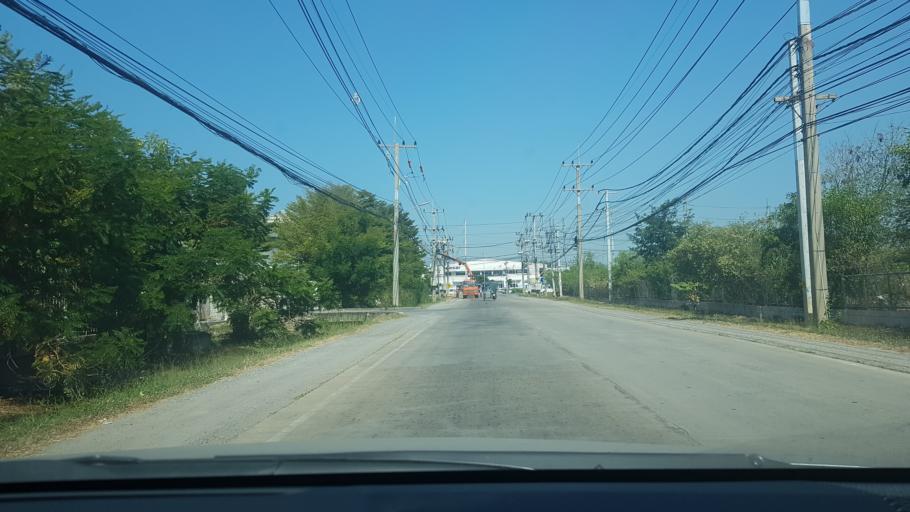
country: TH
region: Phra Nakhon Si Ayutthaya
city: Bang Pa-in
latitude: 14.2507
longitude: 100.6002
